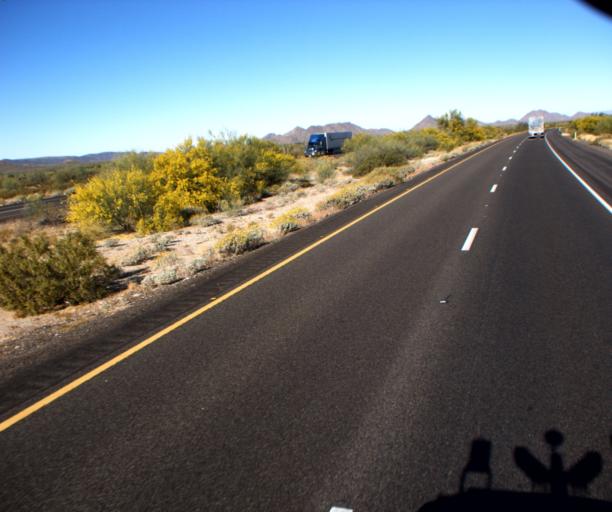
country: US
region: Arizona
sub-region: Maricopa County
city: Gila Bend
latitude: 32.8716
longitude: -112.4374
